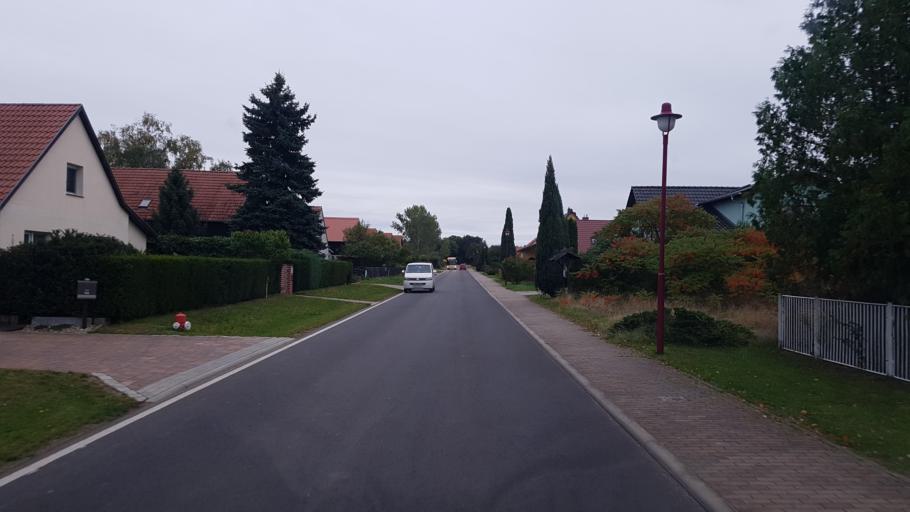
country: DE
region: Brandenburg
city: Kasel-Golzig
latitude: 51.8923
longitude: 13.6490
